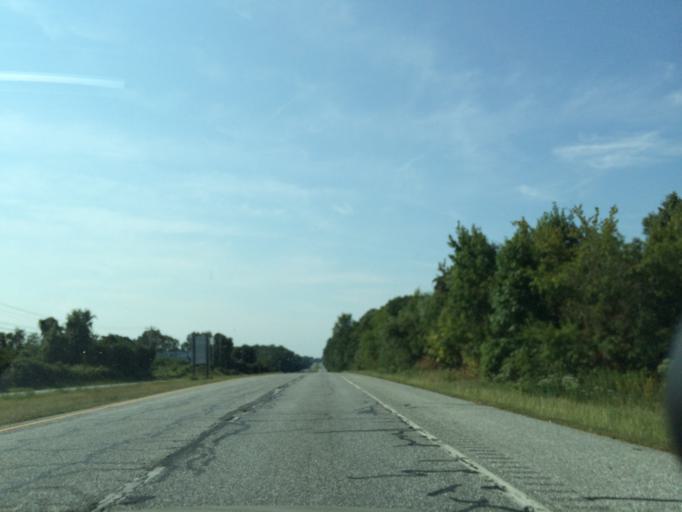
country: US
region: Virginia
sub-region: King George County
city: Dahlgren
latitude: 38.3993
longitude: -76.9533
